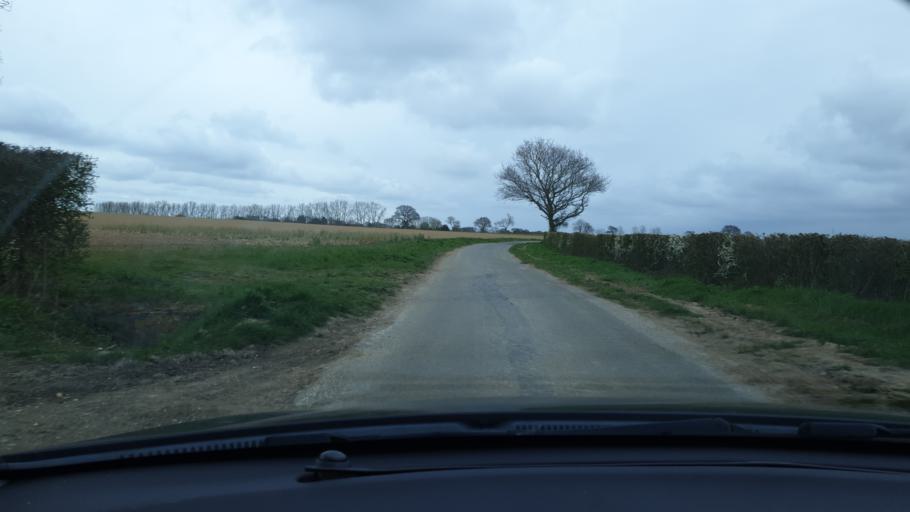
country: GB
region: England
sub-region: Essex
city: Mistley
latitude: 51.8924
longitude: 1.1125
